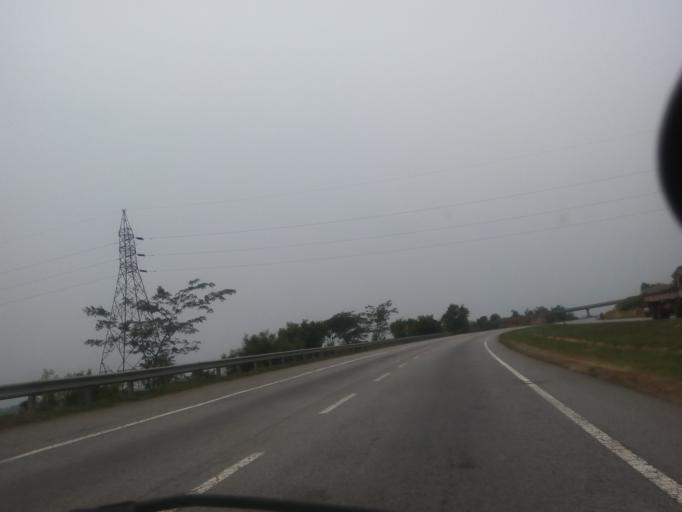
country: IN
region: Karnataka
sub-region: Bangalore Urban
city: Bangalore
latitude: 12.9116
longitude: 77.4673
